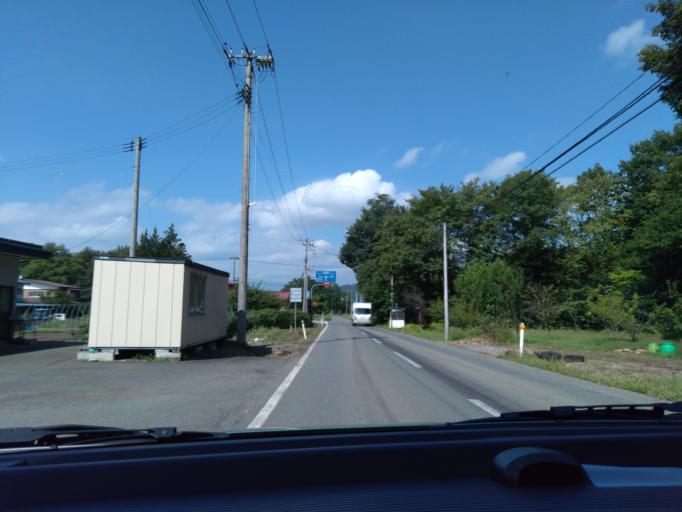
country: JP
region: Iwate
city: Shizukuishi
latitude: 39.6578
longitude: 140.9924
